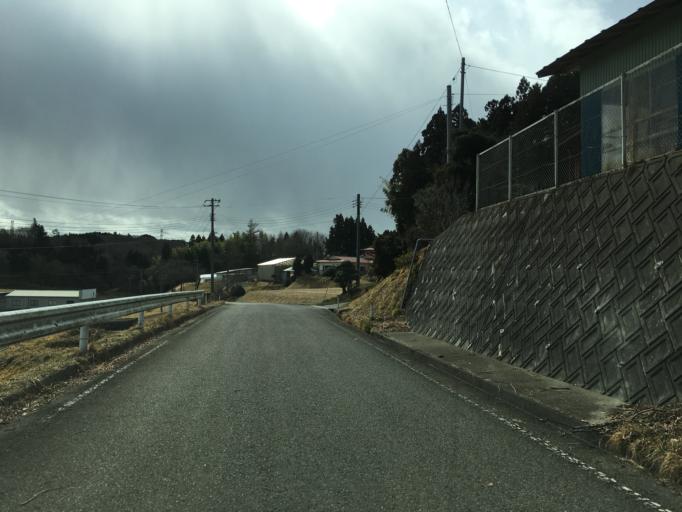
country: JP
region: Fukushima
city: Ishikawa
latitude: 37.1991
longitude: 140.5744
